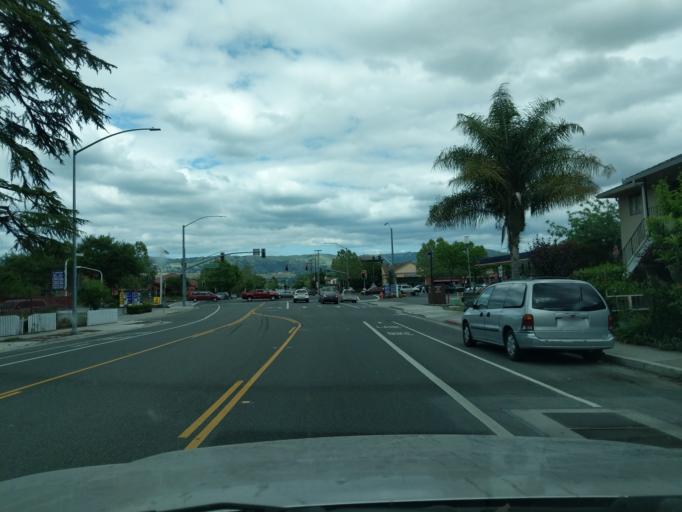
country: US
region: California
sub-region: Santa Clara County
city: Morgan Hill
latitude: 37.1249
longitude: -121.6511
